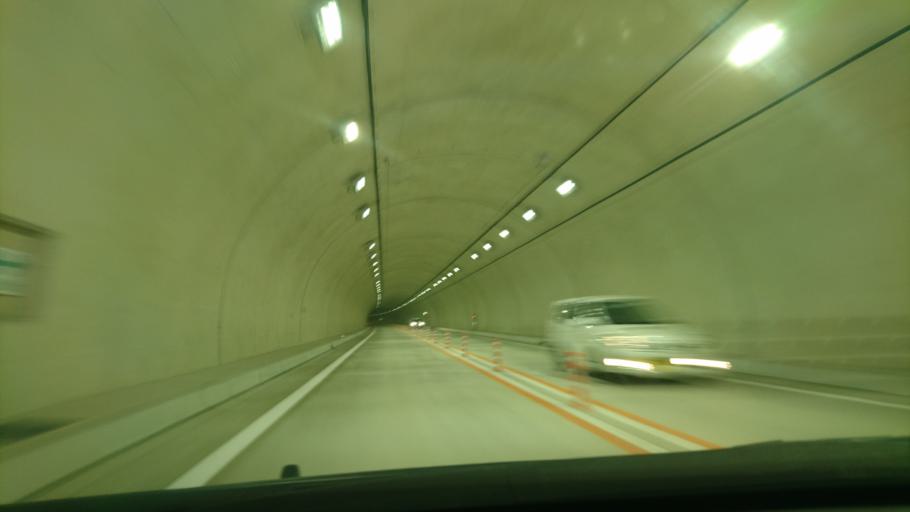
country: JP
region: Iwate
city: Kamaishi
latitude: 39.2792
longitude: 141.8578
